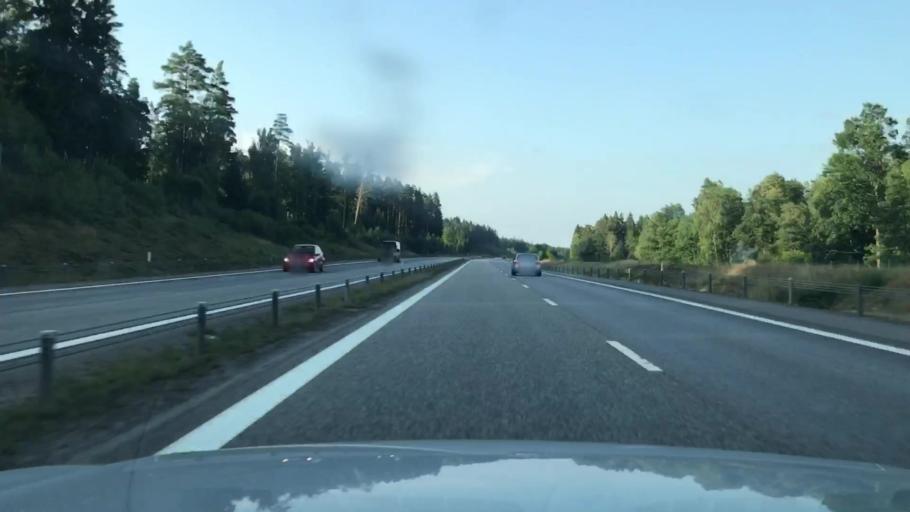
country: SE
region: Kronoberg
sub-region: Markaryds Kommun
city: Stromsnasbruk
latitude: 56.5263
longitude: 13.6839
